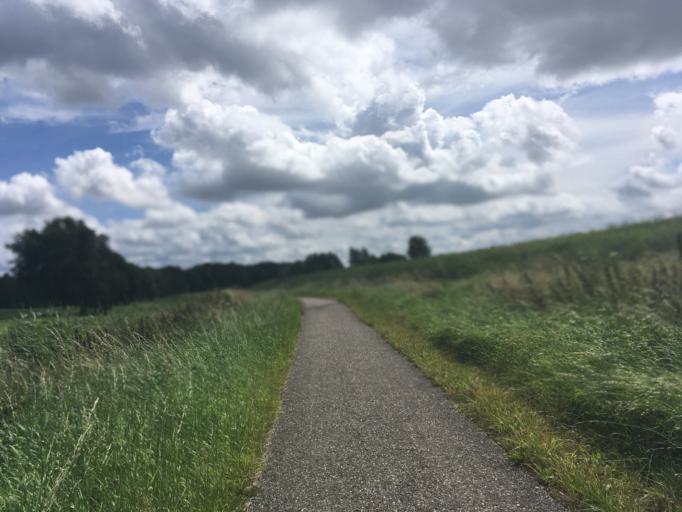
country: NL
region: North Holland
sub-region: Gemeente Haarlem
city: Haarlem
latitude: 52.4033
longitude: 4.7204
